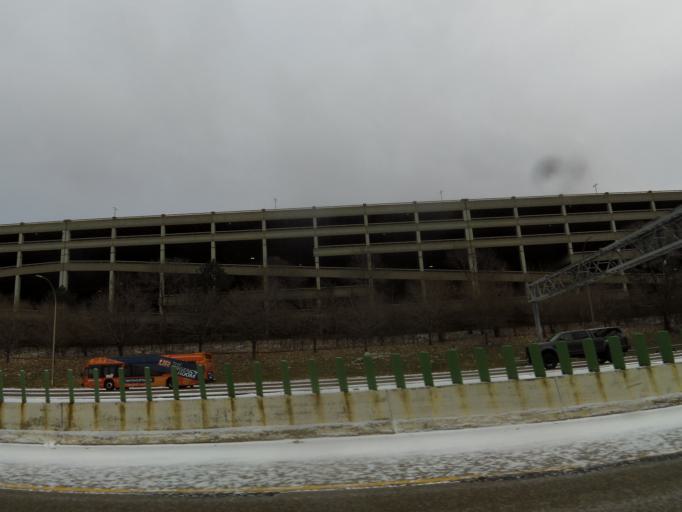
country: US
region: Minnesota
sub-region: Hennepin County
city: Richfield
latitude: 44.8552
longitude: -93.2481
